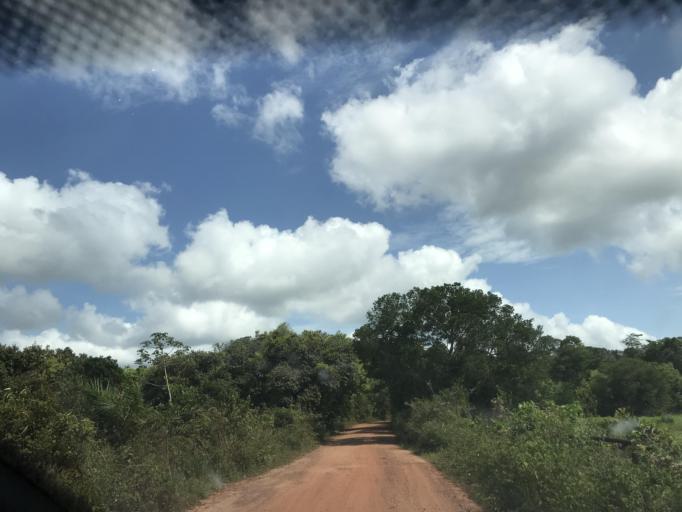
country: BR
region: Bahia
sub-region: Entre Rios
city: Entre Rios
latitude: -12.1625
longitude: -38.0787
